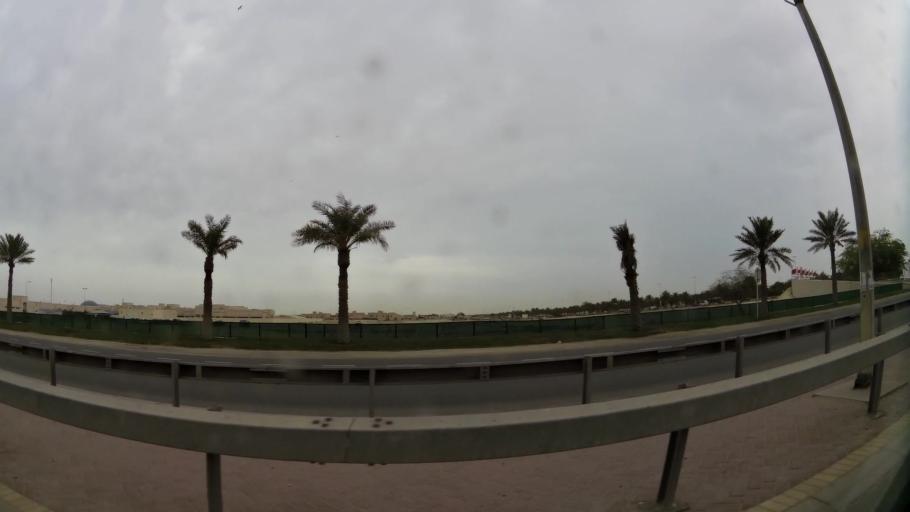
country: BH
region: Northern
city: Ar Rifa'
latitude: 26.0982
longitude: 50.5447
